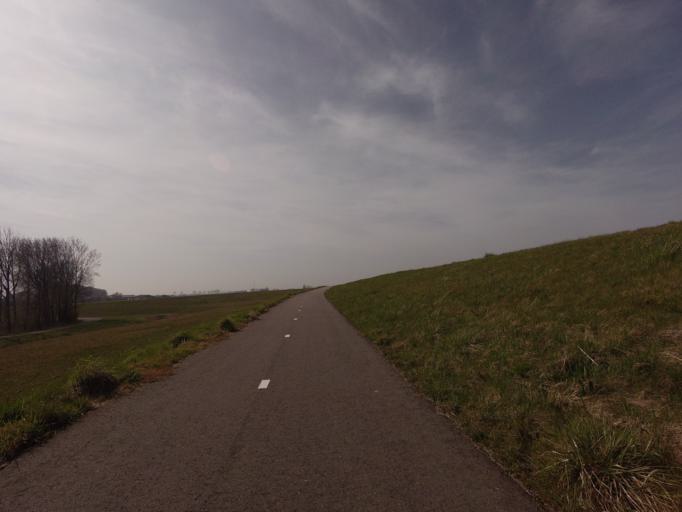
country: NL
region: Zeeland
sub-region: Gemeente Hulst
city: Hulst
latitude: 51.3857
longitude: 4.0220
